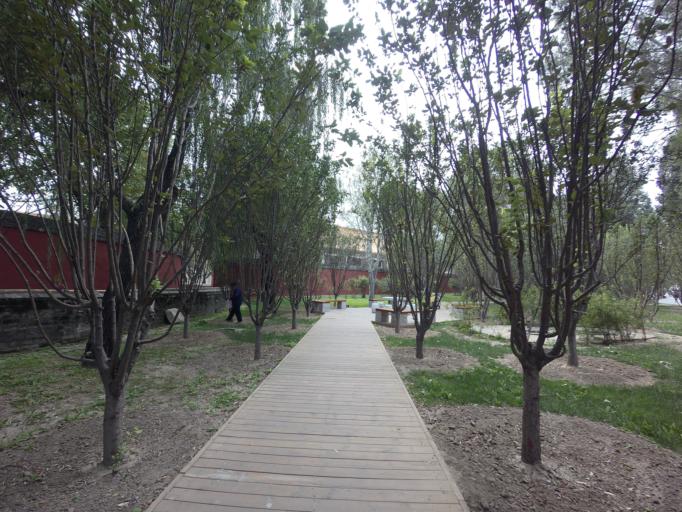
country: CN
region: Beijing
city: Beijing
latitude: 39.9133
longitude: 116.3942
